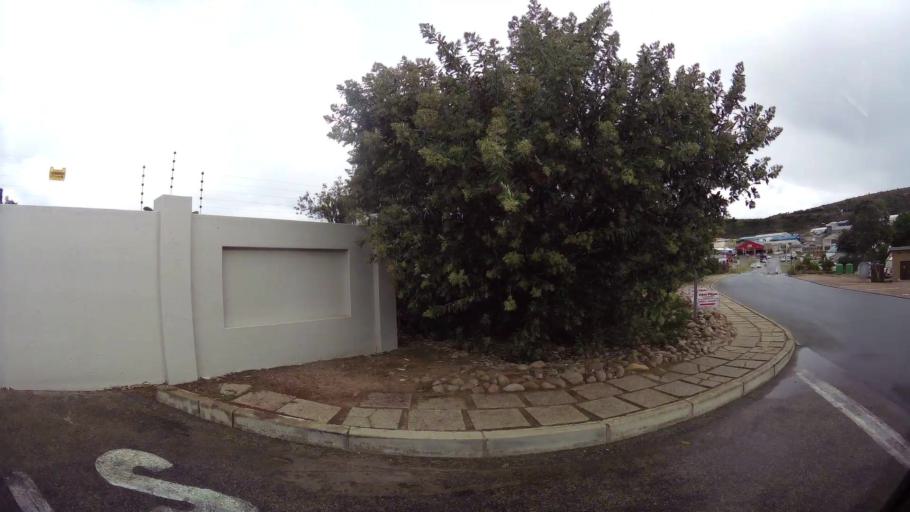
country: ZA
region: Western Cape
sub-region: Eden District Municipality
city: Mossel Bay
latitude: -34.1542
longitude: 22.1043
